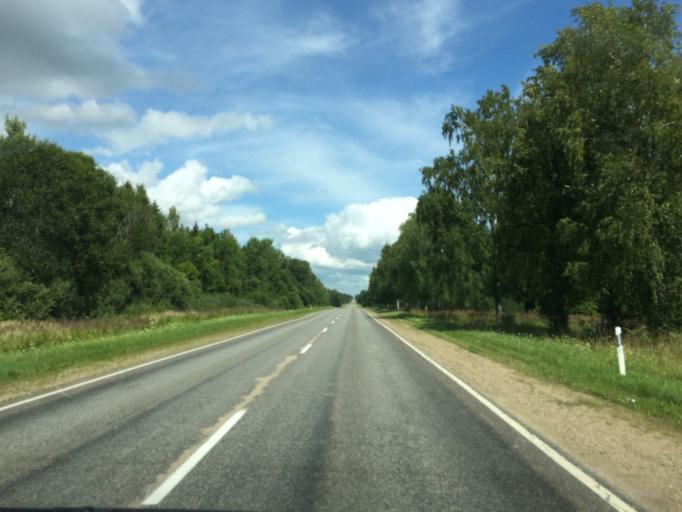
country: LV
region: Rezekne
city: Rezekne
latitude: 56.6358
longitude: 27.4738
